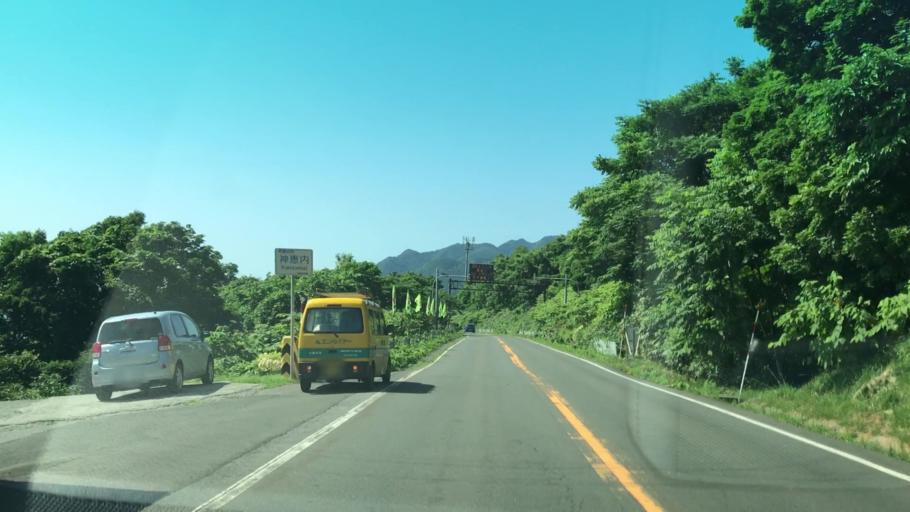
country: JP
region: Hokkaido
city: Iwanai
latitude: 43.1334
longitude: 140.4331
